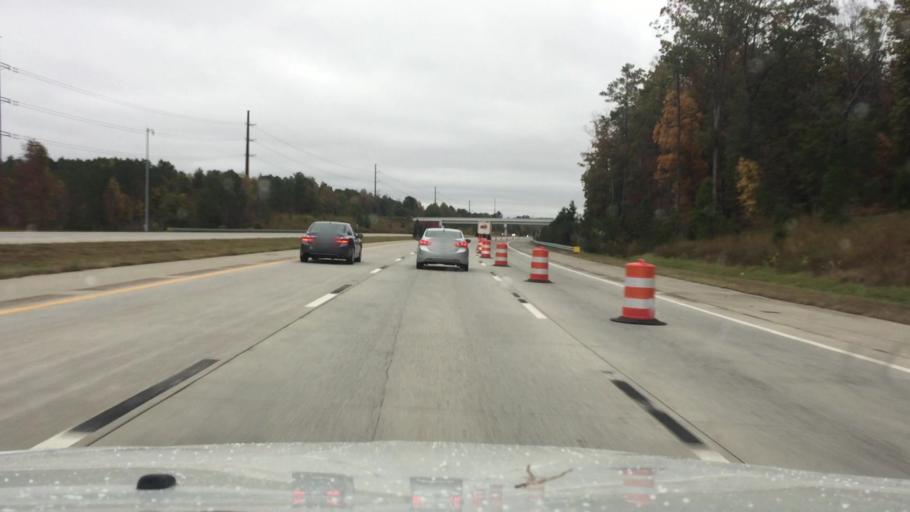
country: US
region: North Carolina
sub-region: Wake County
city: Green Level
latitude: 35.8054
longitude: -78.8919
